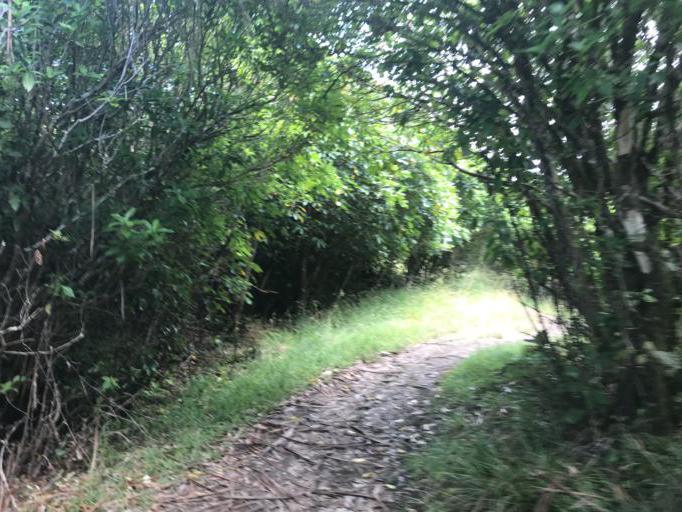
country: NZ
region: Marlborough
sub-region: Marlborough District
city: Picton
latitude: -41.2137
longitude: 173.9911
